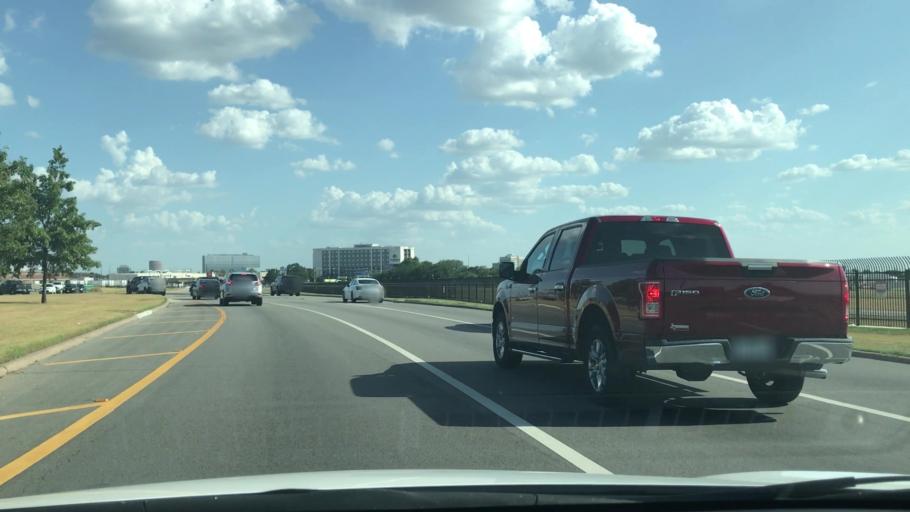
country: US
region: Texas
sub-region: Dallas County
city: University Park
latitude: 32.8406
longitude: -96.8348
